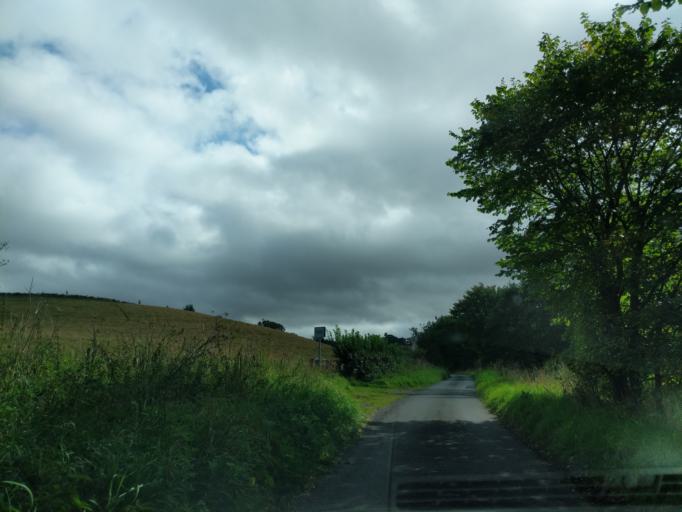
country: GB
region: Scotland
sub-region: The Scottish Borders
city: Kelso
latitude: 55.5661
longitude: -2.4695
